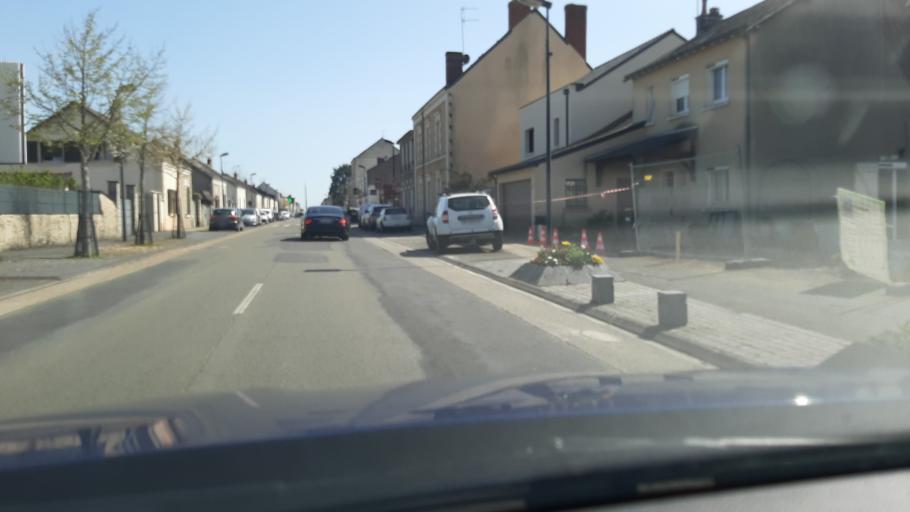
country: FR
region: Pays de la Loire
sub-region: Departement de Maine-et-Loire
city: Les Ponts-de-Ce
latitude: 47.4459
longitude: -0.5048
